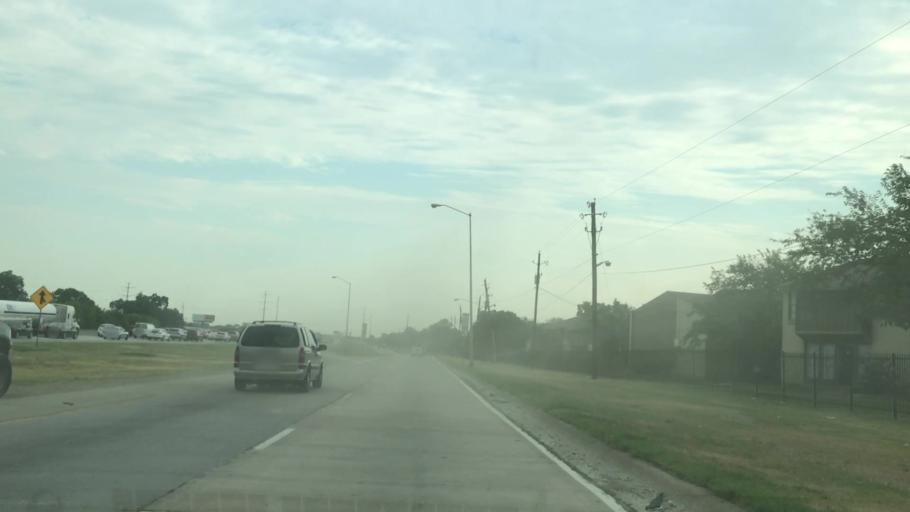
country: US
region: Texas
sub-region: Dallas County
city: Cockrell Hill
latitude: 32.7682
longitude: -96.9144
